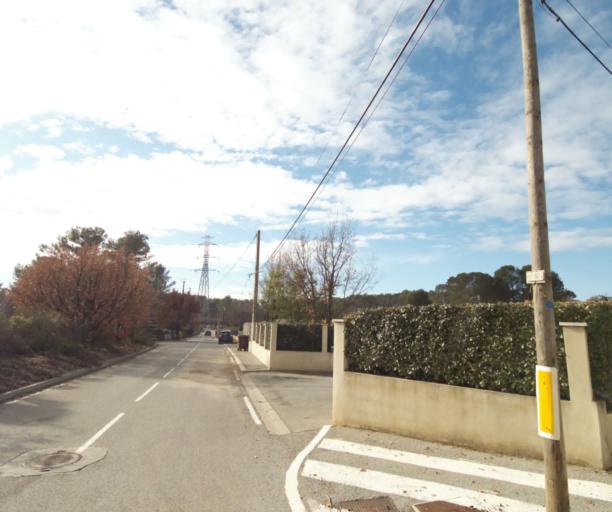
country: FR
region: Provence-Alpes-Cote d'Azur
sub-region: Departement du Var
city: Trans-en-Provence
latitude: 43.5208
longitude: 6.5026
